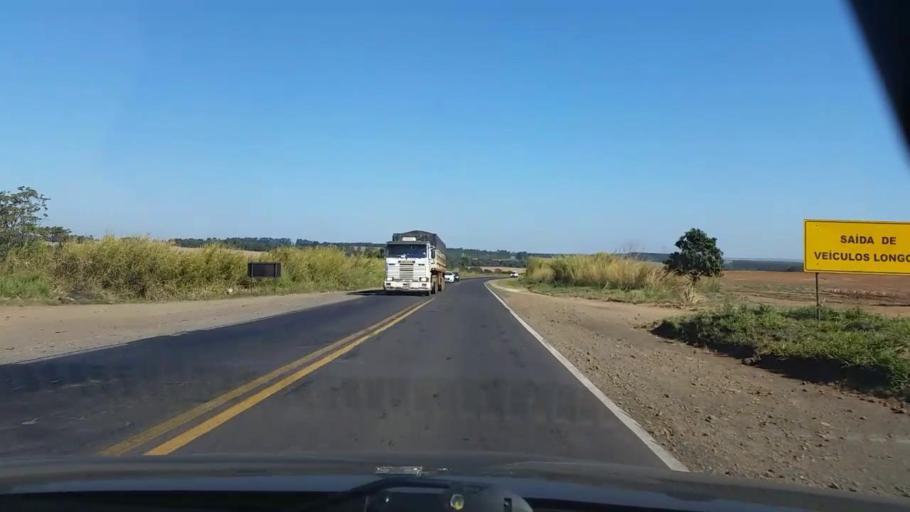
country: BR
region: Sao Paulo
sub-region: Itatinga
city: Itatinga
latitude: -22.9050
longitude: -48.7683
